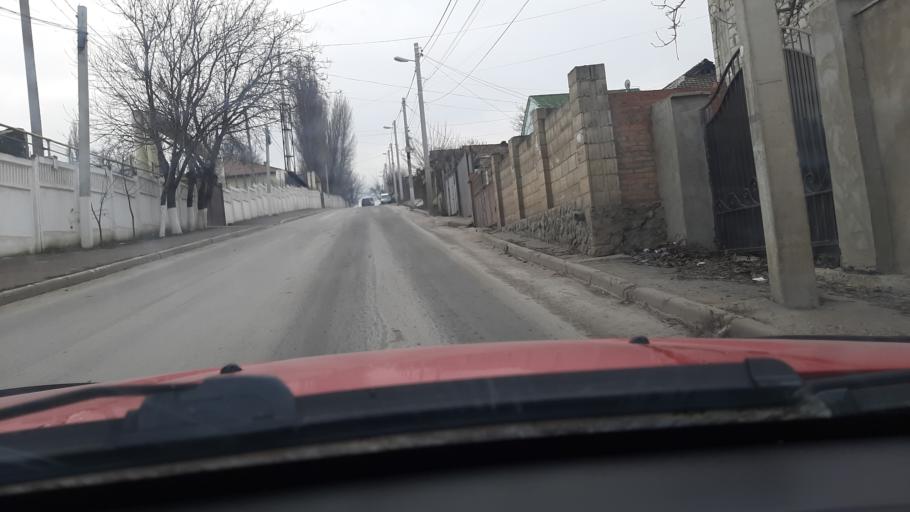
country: MD
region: Chisinau
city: Vatra
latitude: 47.0389
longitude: 28.7926
